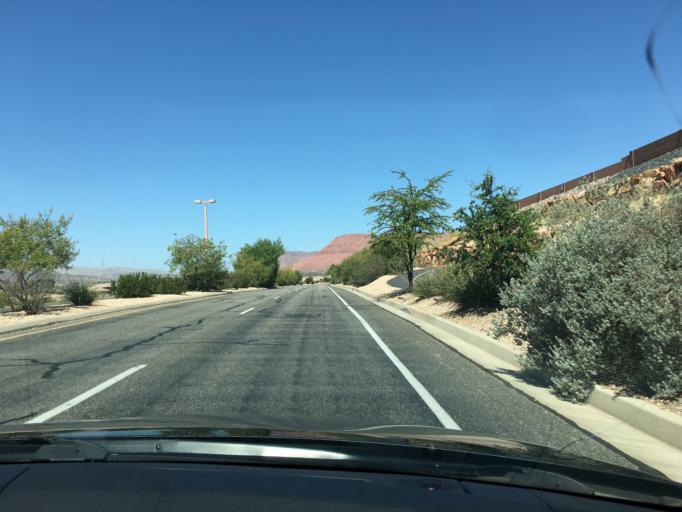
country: US
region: Utah
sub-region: Washington County
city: Santa Clara
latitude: 37.1357
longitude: -113.6169
